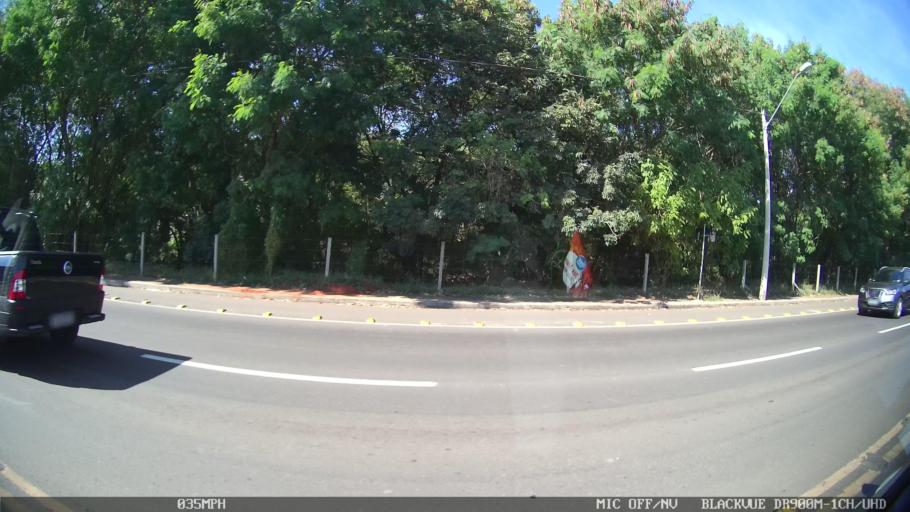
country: BR
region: Sao Paulo
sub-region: Sao Jose Do Rio Preto
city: Sao Jose do Rio Preto
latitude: -20.7917
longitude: -49.3928
